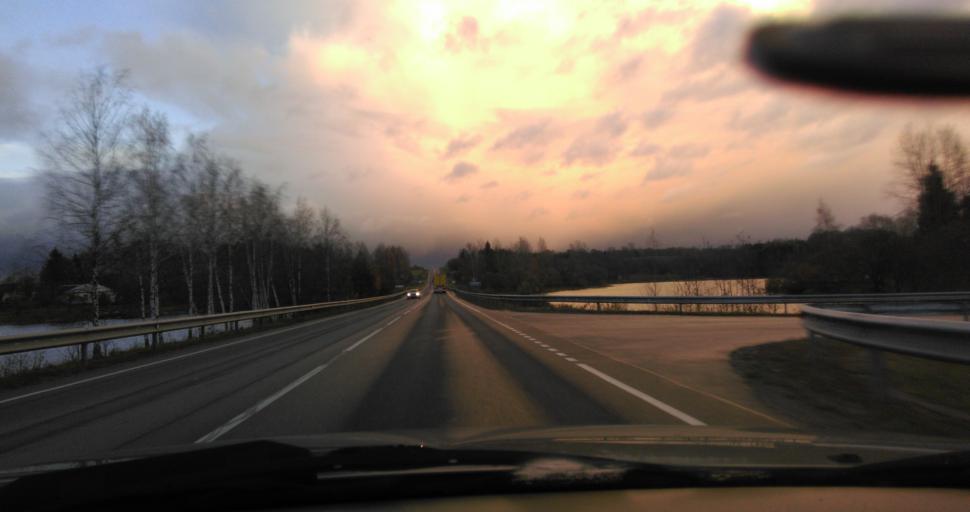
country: LT
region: Utenos apskritis
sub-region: Utena
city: Utena
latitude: 55.5157
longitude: 25.6512
